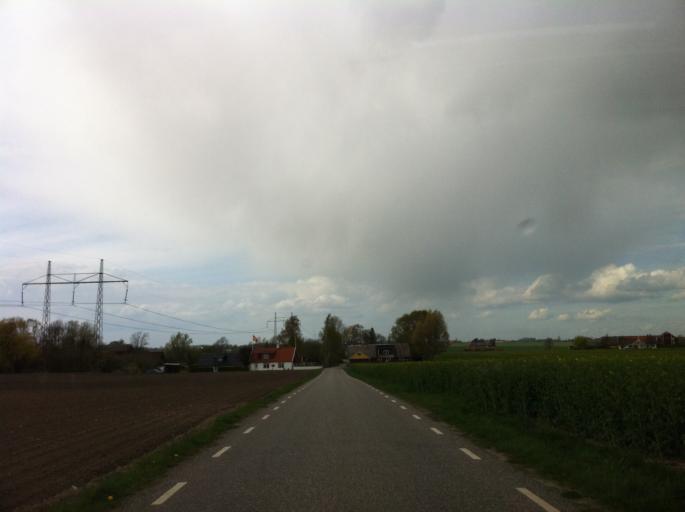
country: SE
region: Skane
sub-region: Svalovs Kommun
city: Teckomatorp
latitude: 55.8531
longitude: 13.0641
